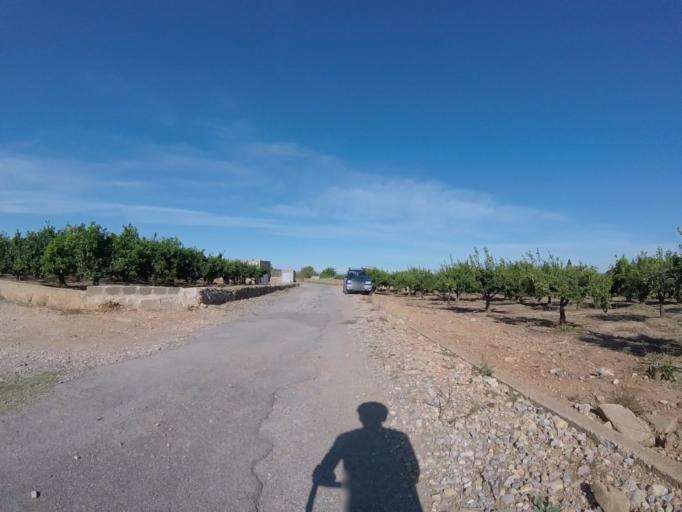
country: ES
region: Valencia
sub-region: Provincia de Castello
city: Torreblanca
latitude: 40.2091
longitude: 0.2342
